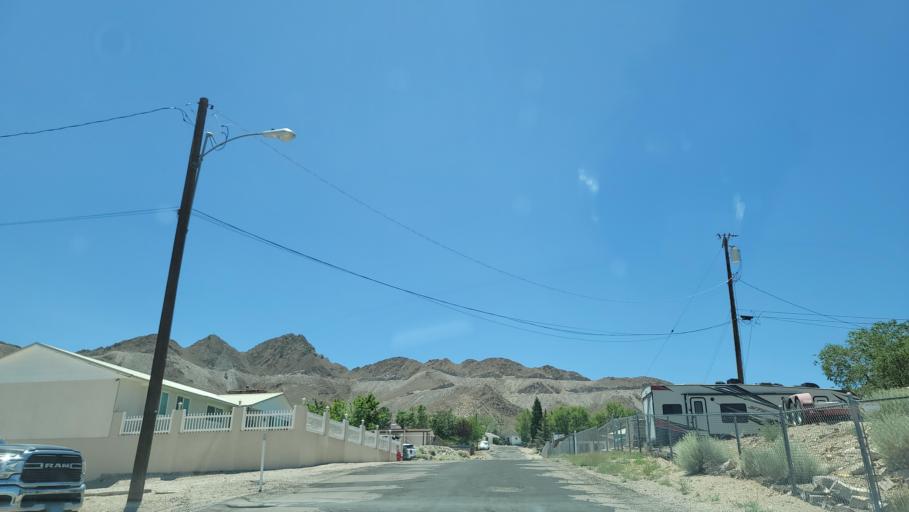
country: US
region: Nevada
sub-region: Nye County
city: Tonopah
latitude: 38.0614
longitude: -117.2300
